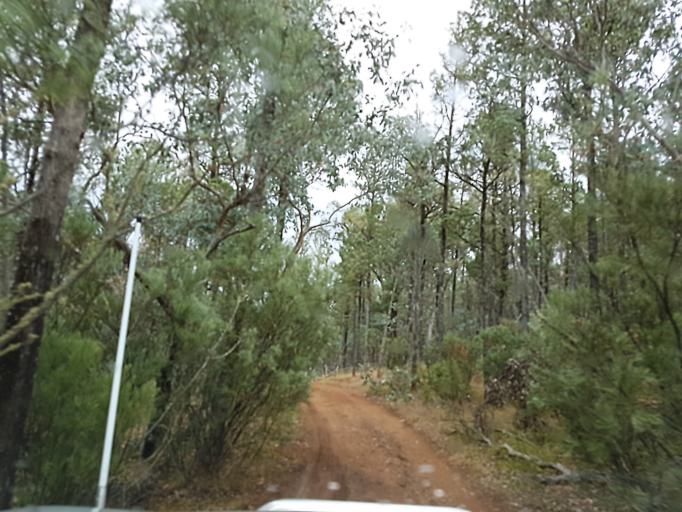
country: AU
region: New South Wales
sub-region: Snowy River
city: Jindabyne
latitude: -36.9448
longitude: 148.3947
